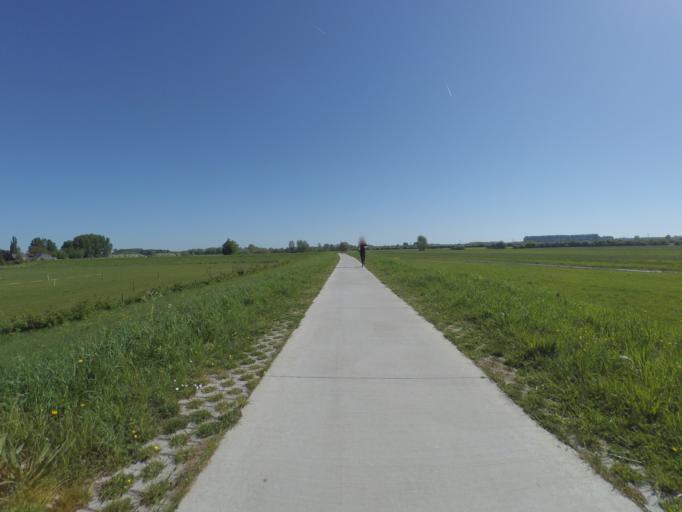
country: NL
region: Gelderland
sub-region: Gemeente Bronckhorst
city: Baak
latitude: 52.1011
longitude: 6.2011
